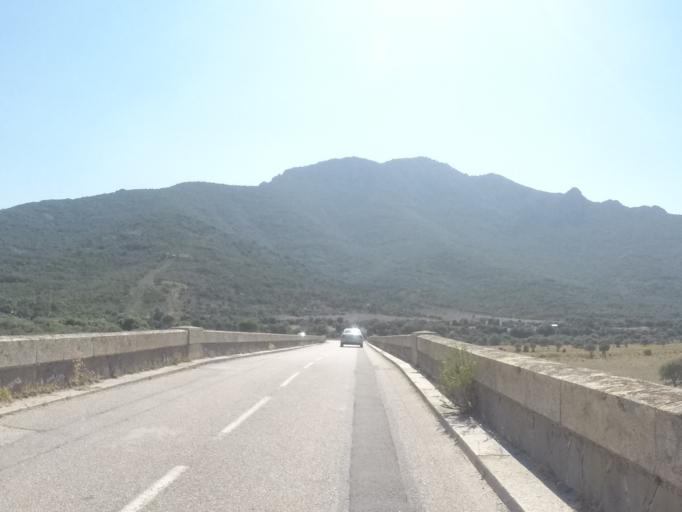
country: FR
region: Corsica
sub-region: Departement de la Haute-Corse
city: Calvi
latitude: 42.4156
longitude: 8.6825
